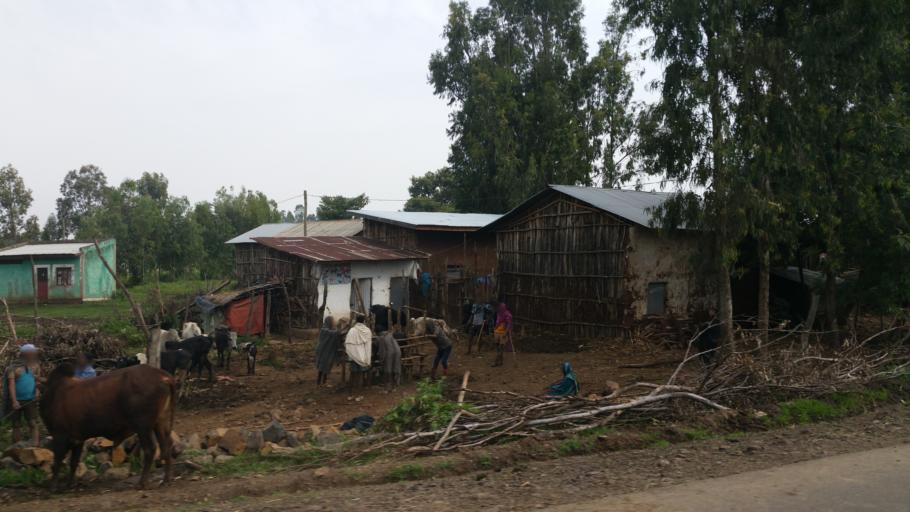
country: ET
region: Amhara
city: Werota
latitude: 11.8363
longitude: 37.6327
